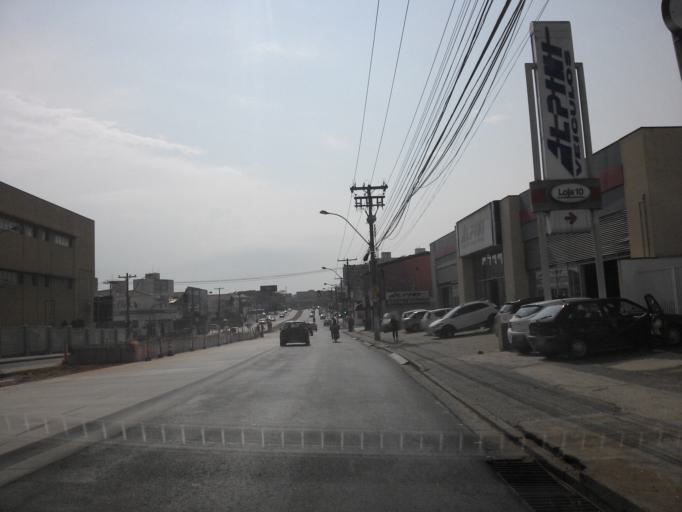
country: BR
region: Sao Paulo
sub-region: Campinas
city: Campinas
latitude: -22.9322
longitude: -47.0895
